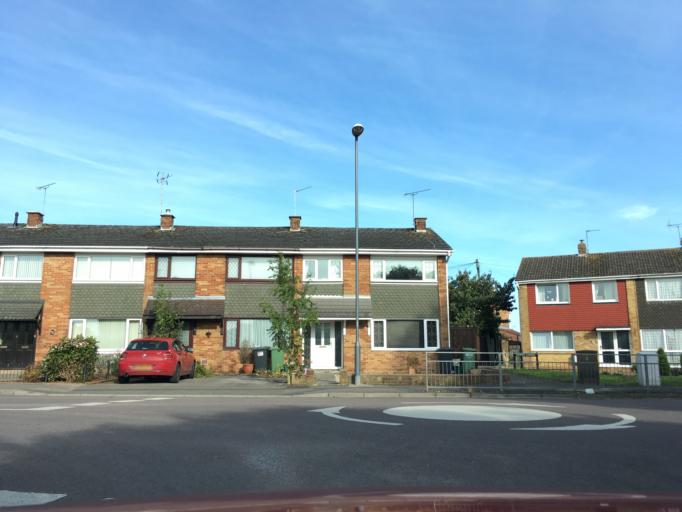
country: GB
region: England
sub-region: South Gloucestershire
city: Yate
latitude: 51.5330
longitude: -2.4167
